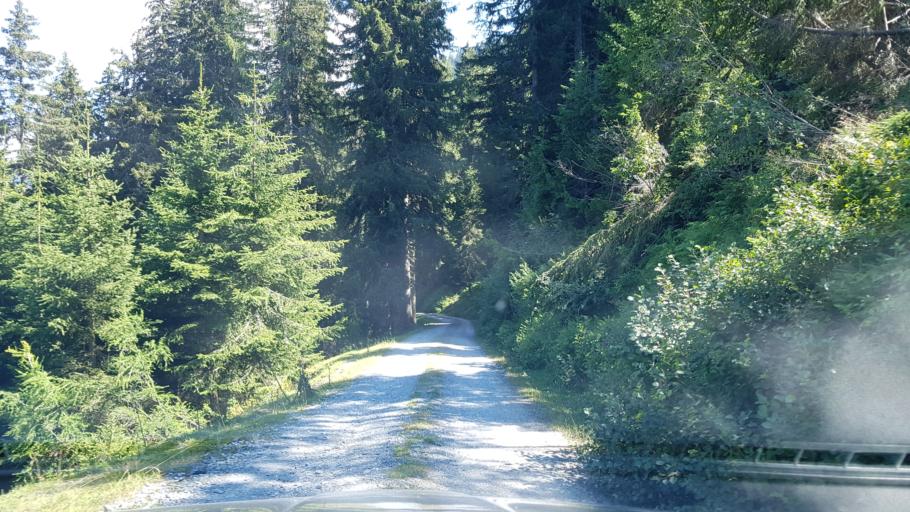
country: AT
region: Salzburg
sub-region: Politischer Bezirk Sankt Johann im Pongau
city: Dorfgastein
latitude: 47.2428
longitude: 13.0735
